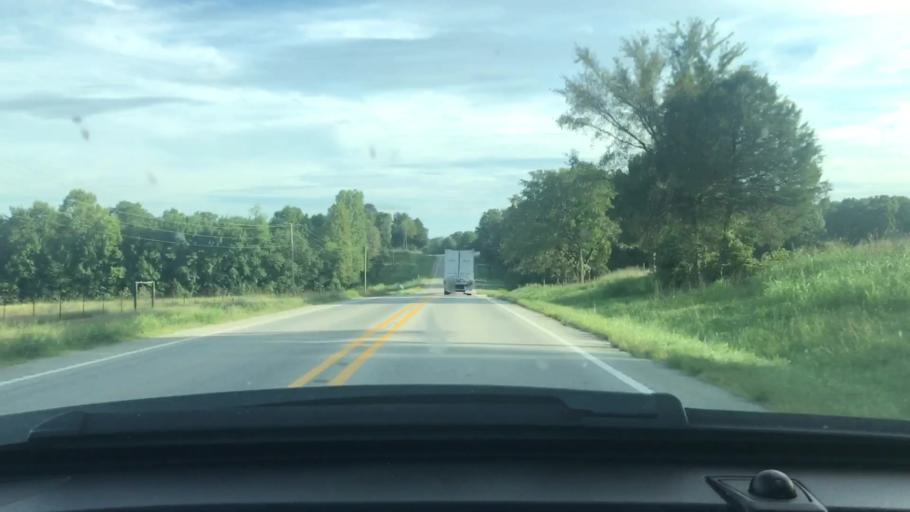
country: US
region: Arkansas
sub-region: Lawrence County
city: Hoxie
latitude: 36.1589
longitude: -91.1620
